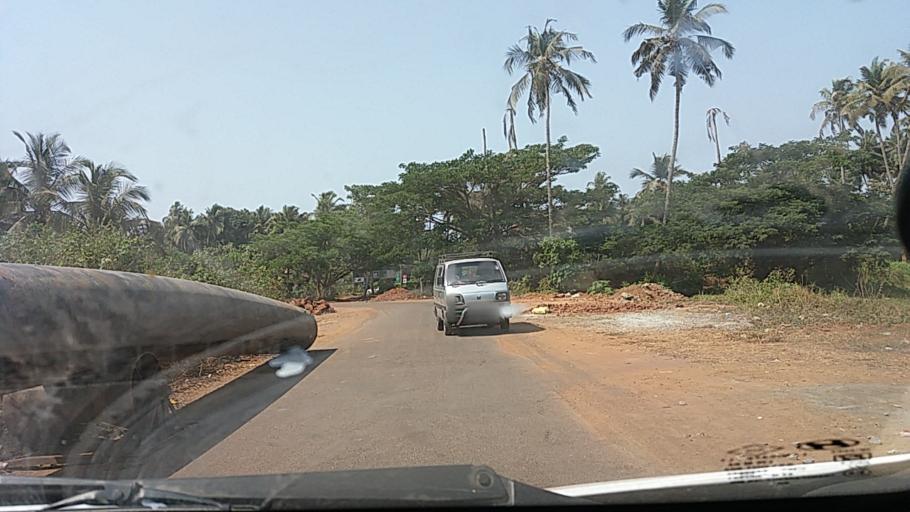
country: IN
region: Goa
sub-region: South Goa
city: Madgaon
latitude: 15.2818
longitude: 73.9552
